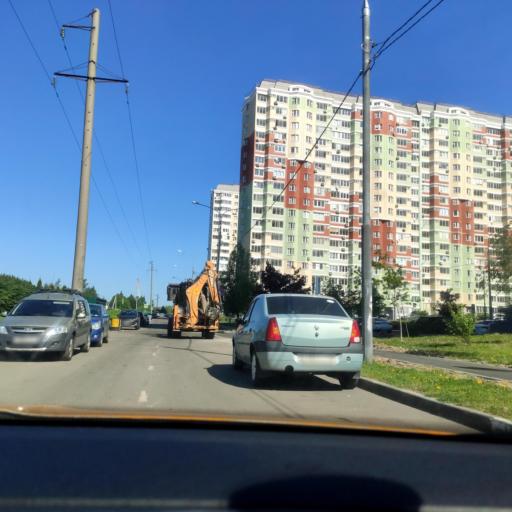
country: RU
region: Moskovskaya
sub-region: Leninskiy Rayon
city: Vnukovo
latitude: 55.6214
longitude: 37.3020
